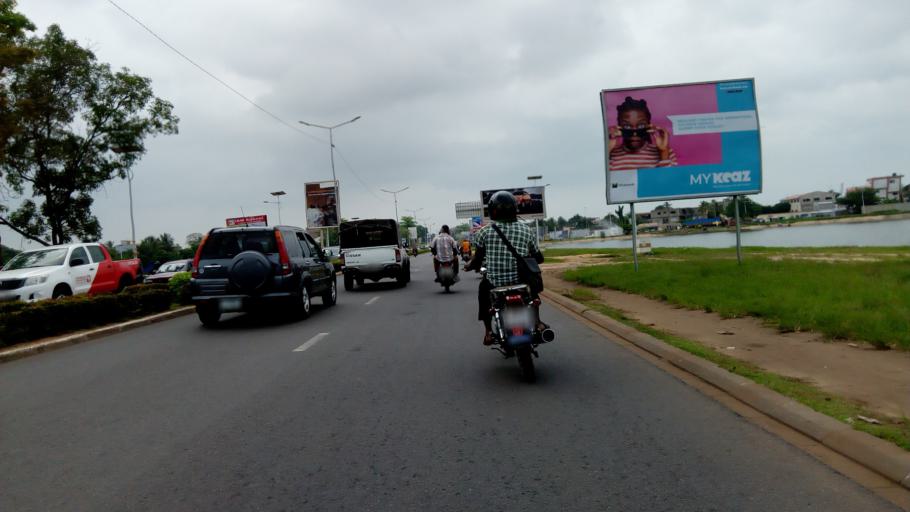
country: TG
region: Maritime
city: Lome
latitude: 6.1675
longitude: 1.2217
